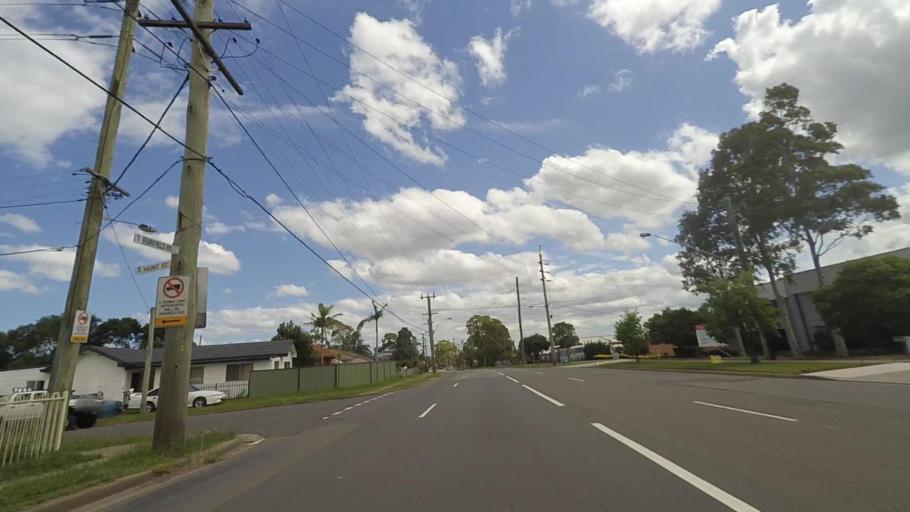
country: AU
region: New South Wales
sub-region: Holroyd
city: Guildford West
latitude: -33.8518
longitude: 150.9605
